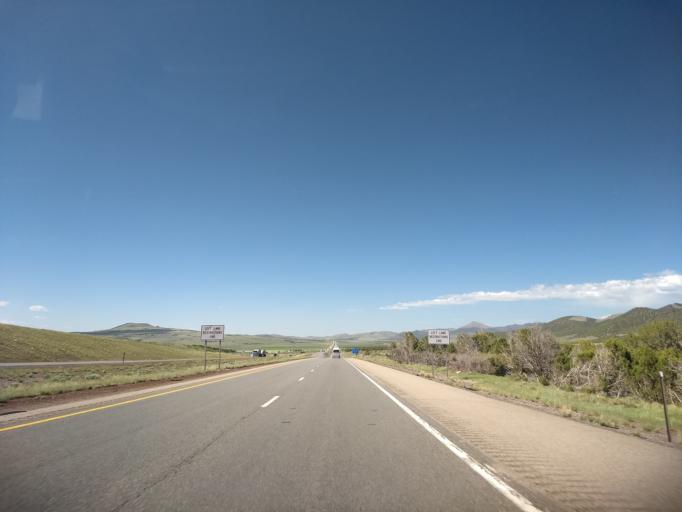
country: US
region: Utah
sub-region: Beaver County
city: Beaver
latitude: 38.4906
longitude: -112.6176
